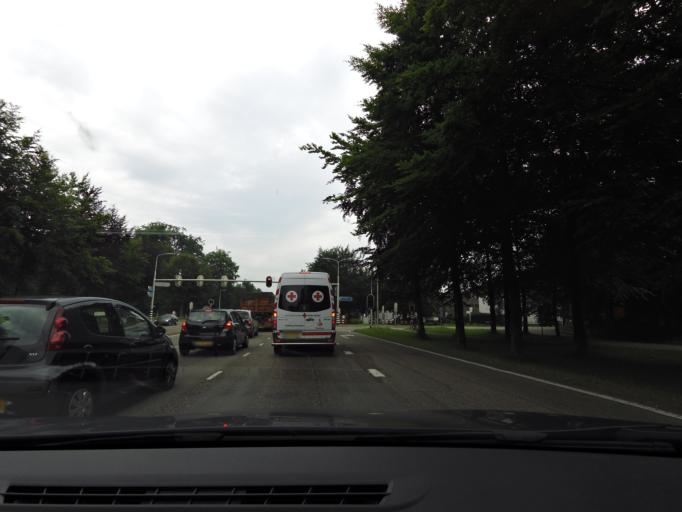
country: NL
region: Gelderland
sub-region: Gemeente Rheden
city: Dieren
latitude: 52.0404
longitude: 6.1003
